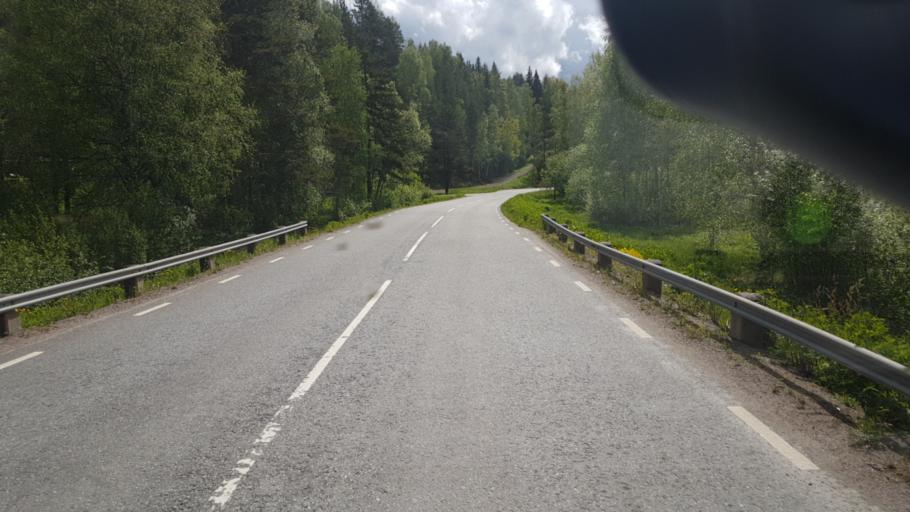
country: NO
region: Ostfold
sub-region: Romskog
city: Romskog
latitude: 59.6978
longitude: 12.0866
